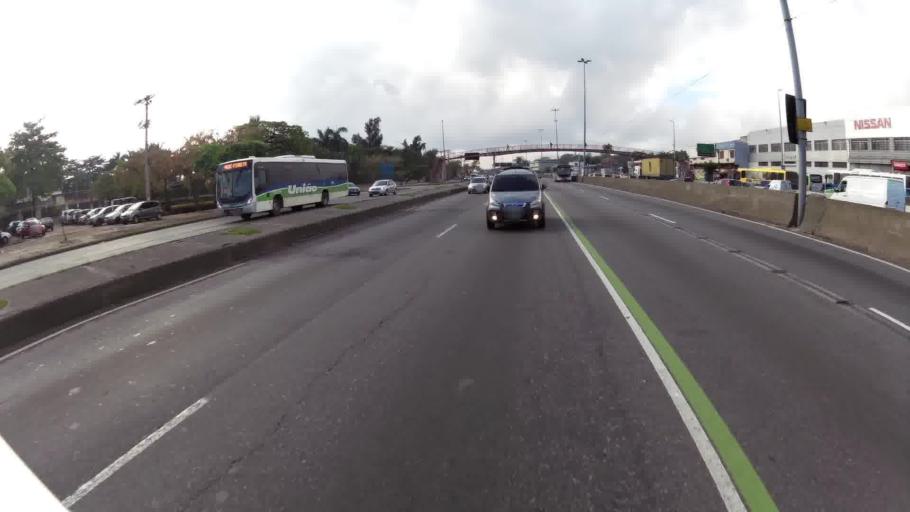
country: BR
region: Rio de Janeiro
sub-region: Duque De Caxias
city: Duque de Caxias
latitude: -22.8294
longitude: -43.2712
